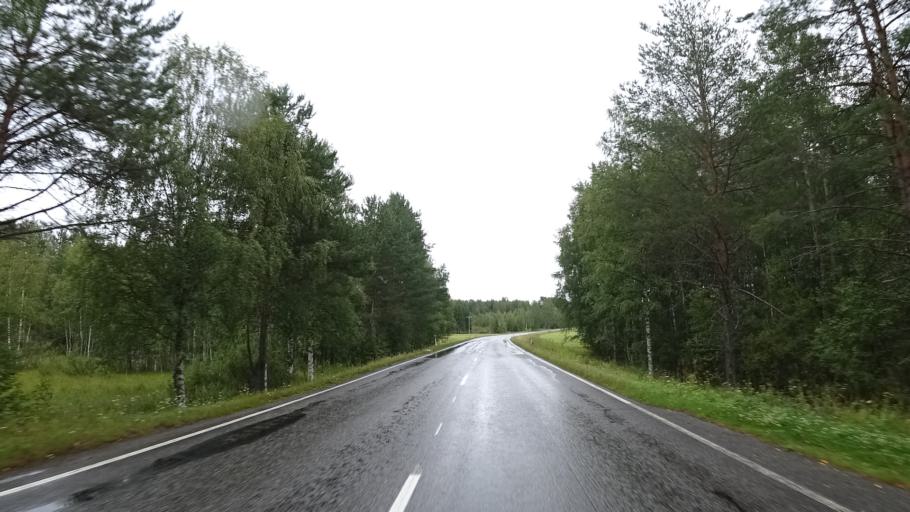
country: FI
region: Southern Savonia
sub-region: Savonlinna
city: Kerimaeki
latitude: 62.0343
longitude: 29.5198
